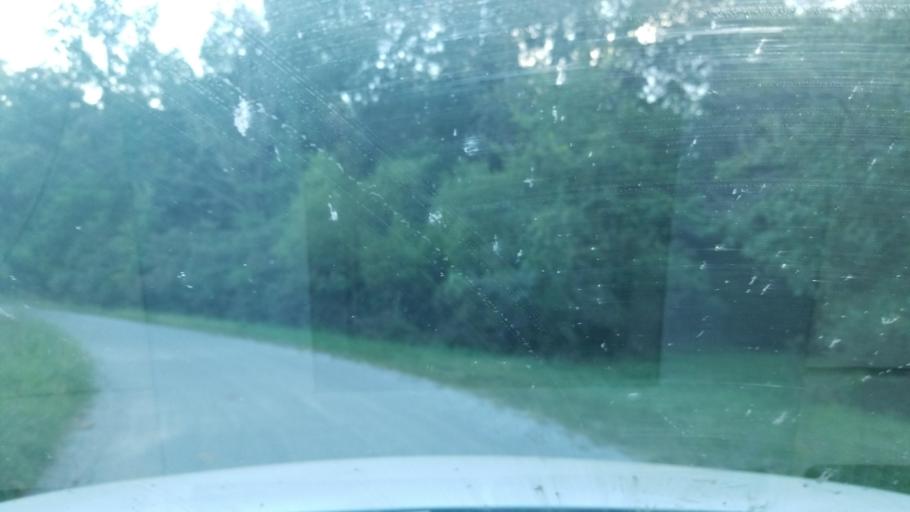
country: US
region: Illinois
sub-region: Saline County
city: Carrier Mills
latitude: 37.7902
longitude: -88.7051
